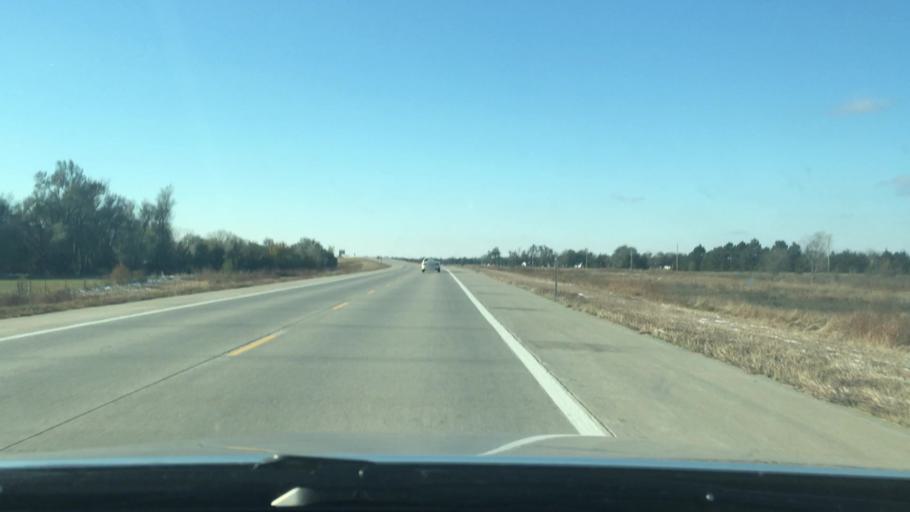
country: US
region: Kansas
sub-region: Reno County
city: Hutchinson
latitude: 38.0985
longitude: -98.0075
